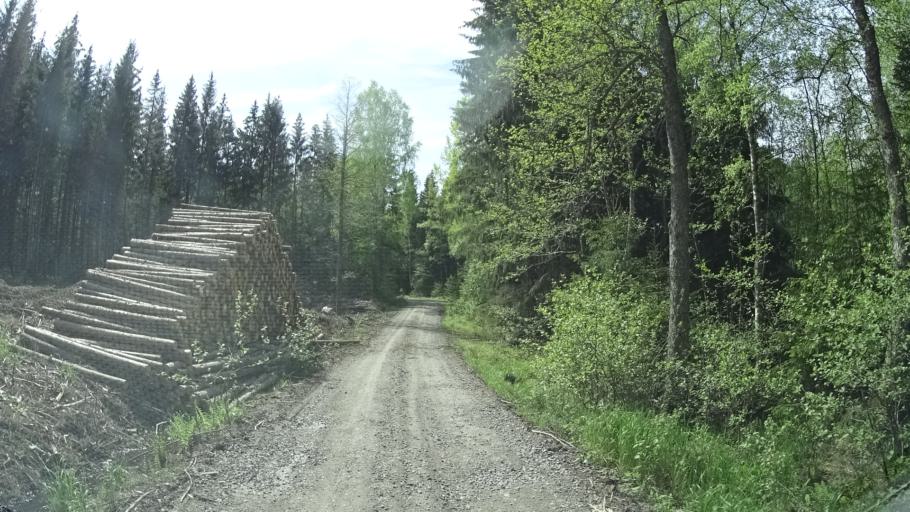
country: SE
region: OEstergoetland
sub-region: Finspangs Kommun
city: Finspang
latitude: 58.7907
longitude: 15.8443
